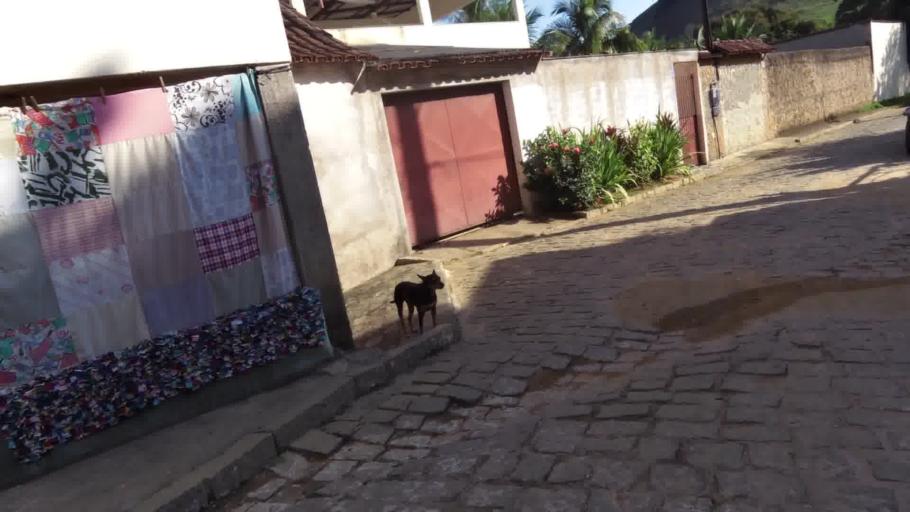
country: BR
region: Espirito Santo
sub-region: Alfredo Chaves
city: Alfredo Chaves
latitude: -20.6300
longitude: -40.7627
